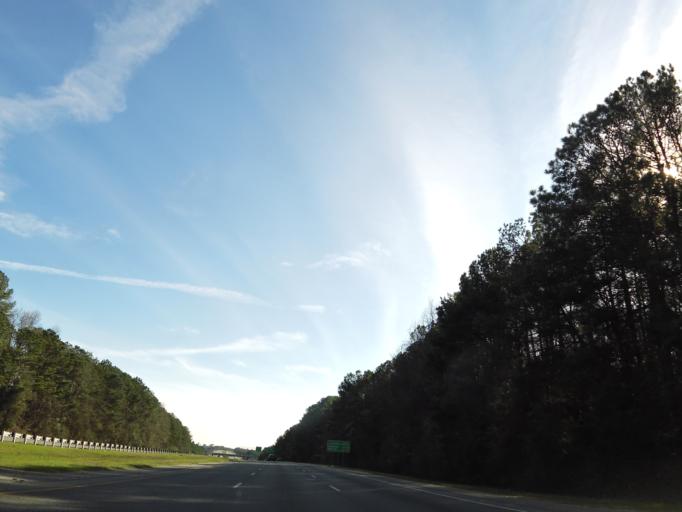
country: US
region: Alabama
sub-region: Russell County
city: Phenix City
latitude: 32.5561
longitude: -84.9628
